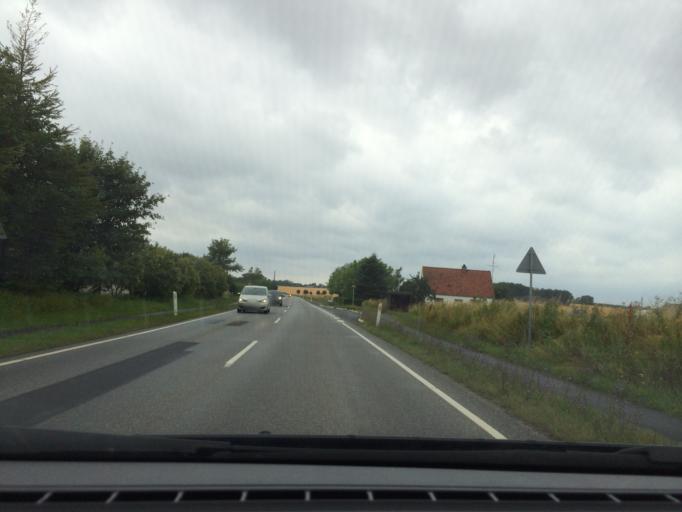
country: DK
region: Zealand
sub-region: Vordingborg Kommune
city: Stege
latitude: 54.9951
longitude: 12.3094
